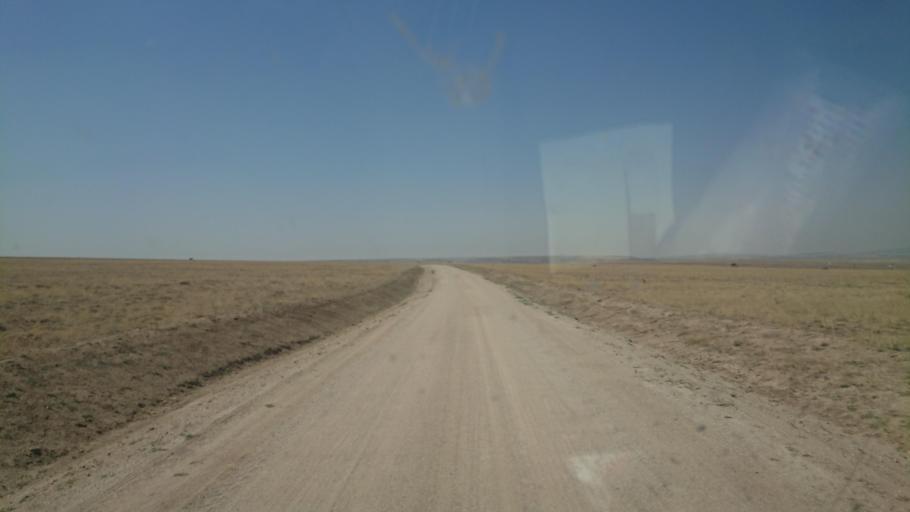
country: TR
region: Aksaray
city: Agacoren
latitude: 38.7459
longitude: 33.8975
